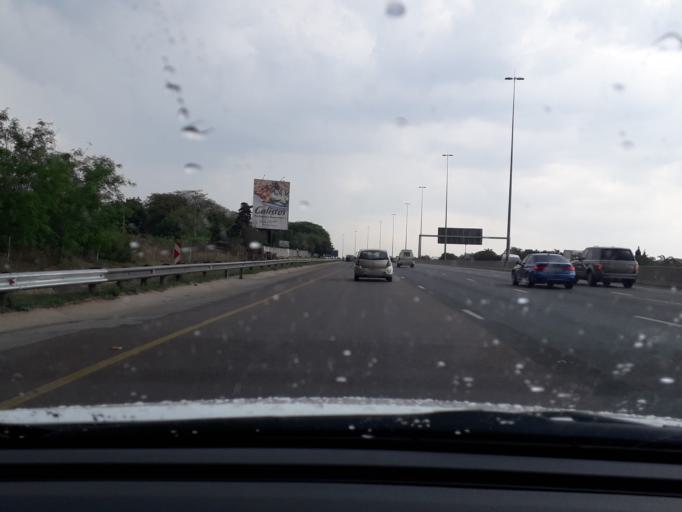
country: ZA
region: Gauteng
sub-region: City of Johannesburg Metropolitan Municipality
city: Roodepoort
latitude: -26.1217
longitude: 27.9464
